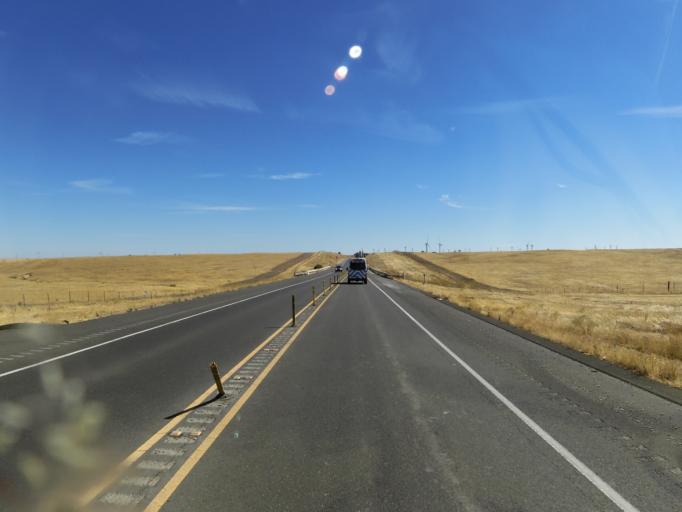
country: US
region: California
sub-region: Solano County
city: Suisun
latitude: 38.2156
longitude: -121.8842
